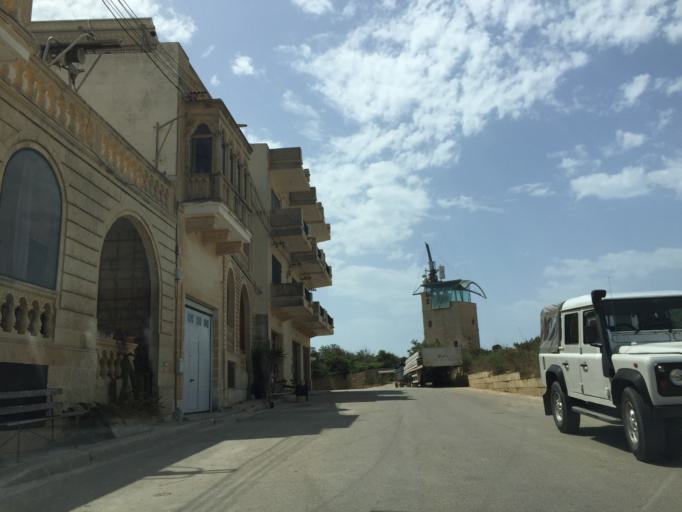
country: MT
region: Ghajnsielem
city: Ghajnsielem
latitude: 36.0365
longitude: 14.2839
